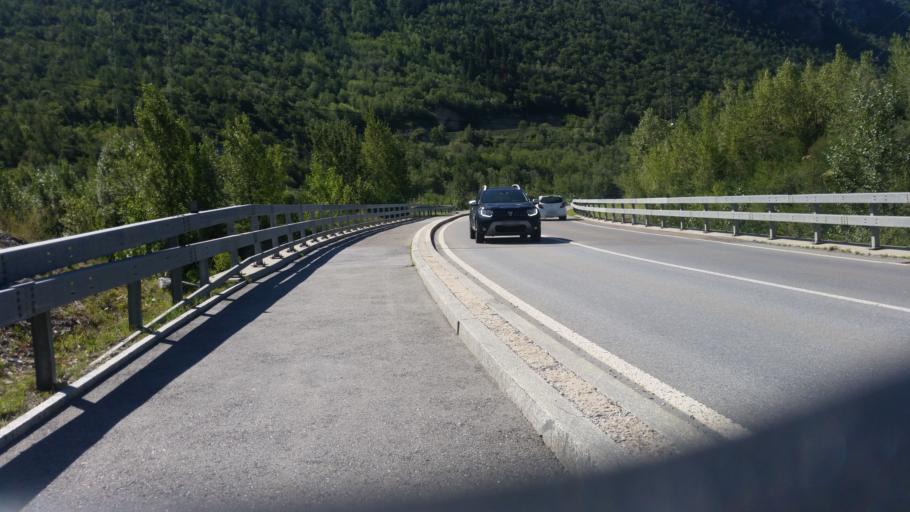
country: CH
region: Valais
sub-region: Sierre District
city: Chippis
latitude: 46.2908
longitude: 7.5606
